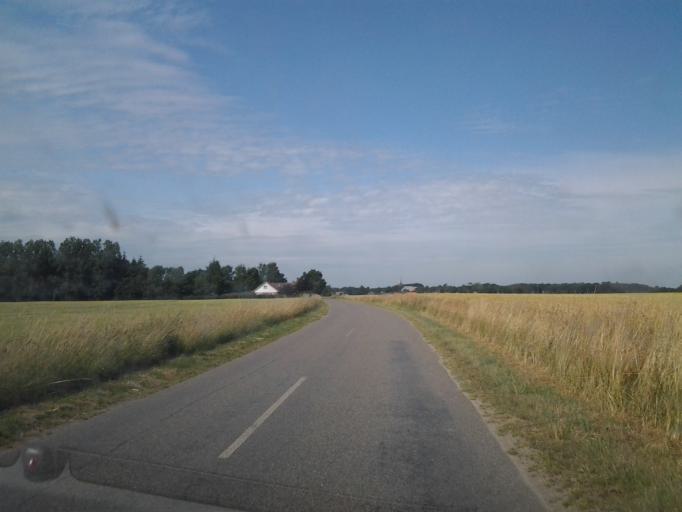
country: DE
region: Schleswig-Holstein
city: Aventoft
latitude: 54.9276
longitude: 8.7979
